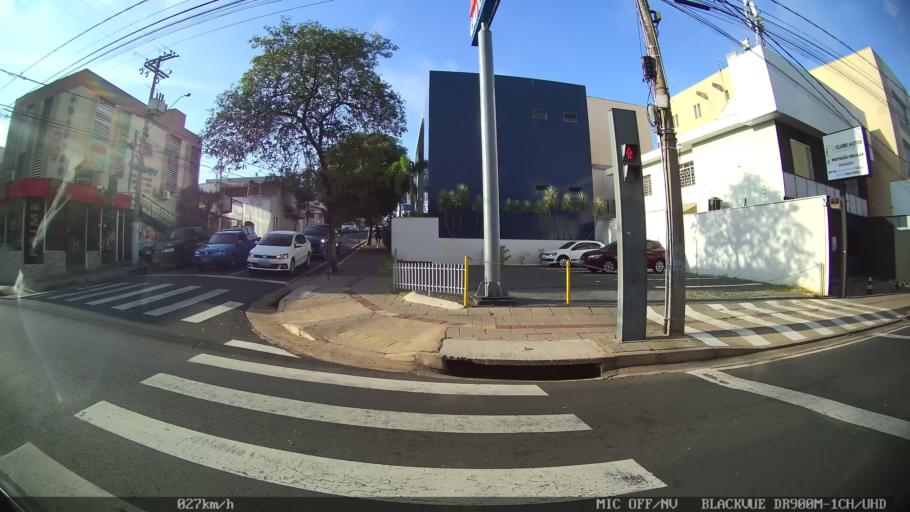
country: BR
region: Sao Paulo
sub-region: Sao Jose Do Rio Preto
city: Sao Jose do Rio Preto
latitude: -20.8148
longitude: -49.3788
